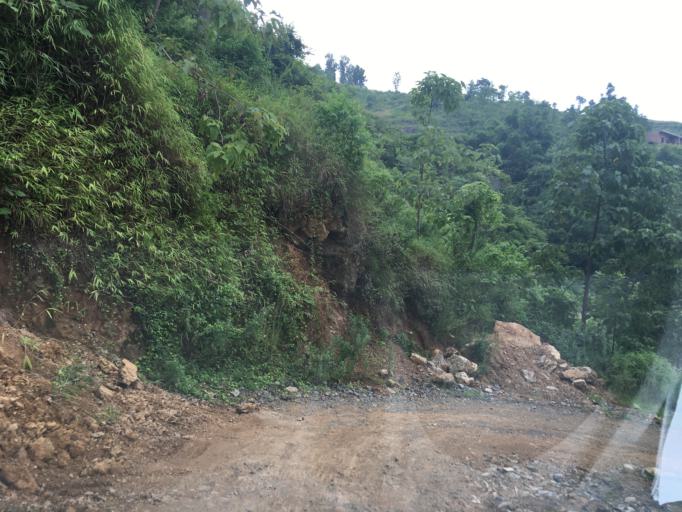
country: CN
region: Guangxi Zhuangzu Zizhiqu
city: Xinzhou
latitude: 25.1713
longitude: 105.7319
